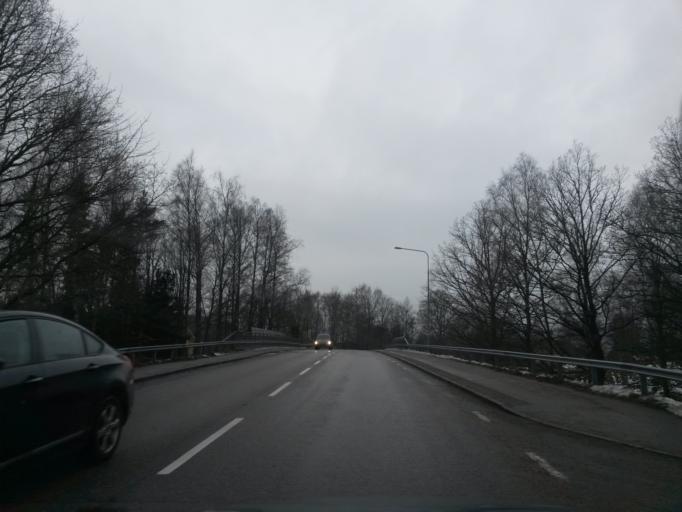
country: SE
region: Vaestra Goetaland
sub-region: Vanersborgs Kommun
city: Vargon
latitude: 58.3519
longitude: 12.4179
